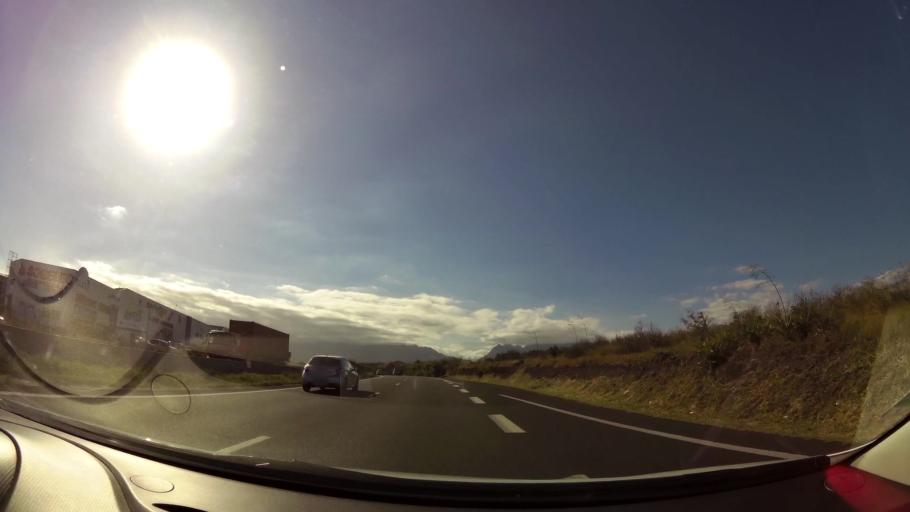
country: RE
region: Reunion
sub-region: Reunion
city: Saint-Pierre
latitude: -21.3210
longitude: 55.4465
